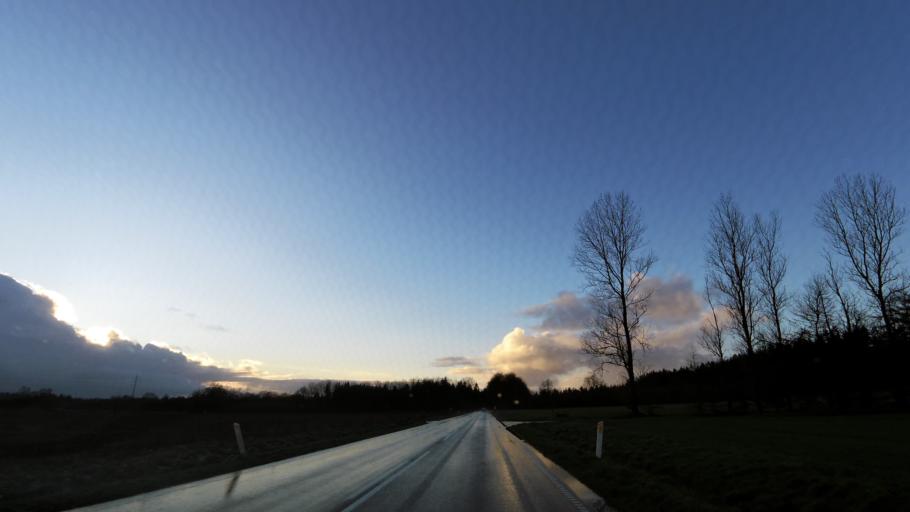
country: DK
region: Central Jutland
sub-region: Ikast-Brande Kommune
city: Brande
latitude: 56.0089
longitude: 9.0846
